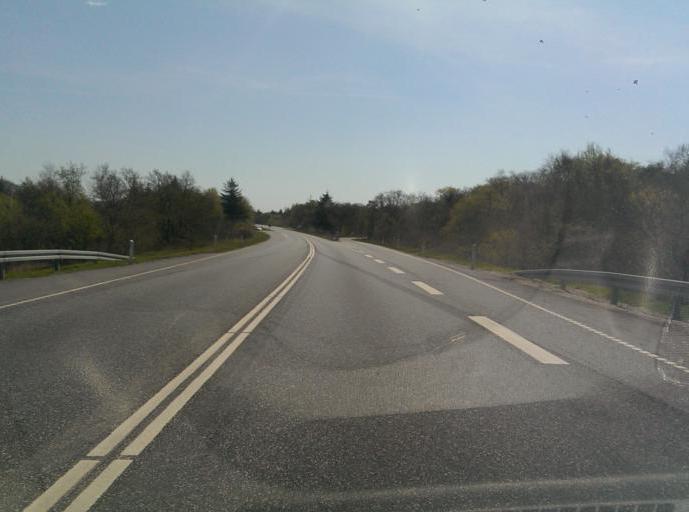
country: DK
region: South Denmark
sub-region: Esbjerg Kommune
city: Ribe
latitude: 55.3924
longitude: 8.7360
